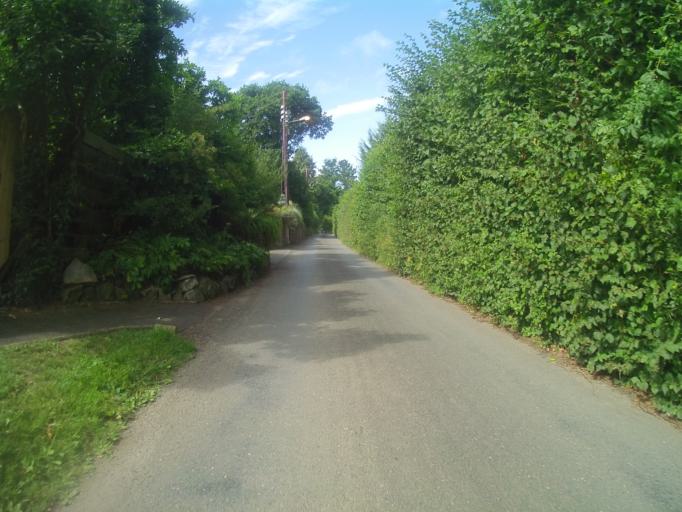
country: GB
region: England
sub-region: Devon
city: Buckfastleigh
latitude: 50.4930
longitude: -3.7828
